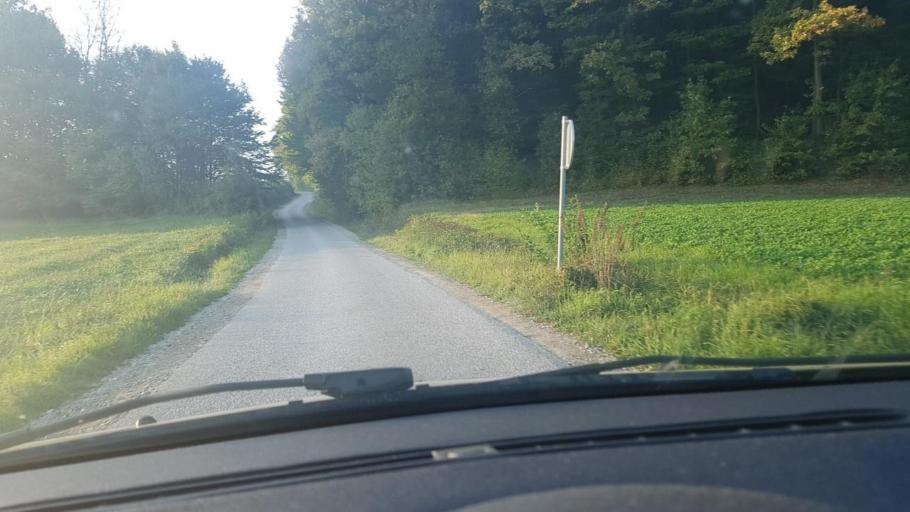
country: SI
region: Majsperk
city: Majsperk
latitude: 46.3314
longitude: 15.7280
